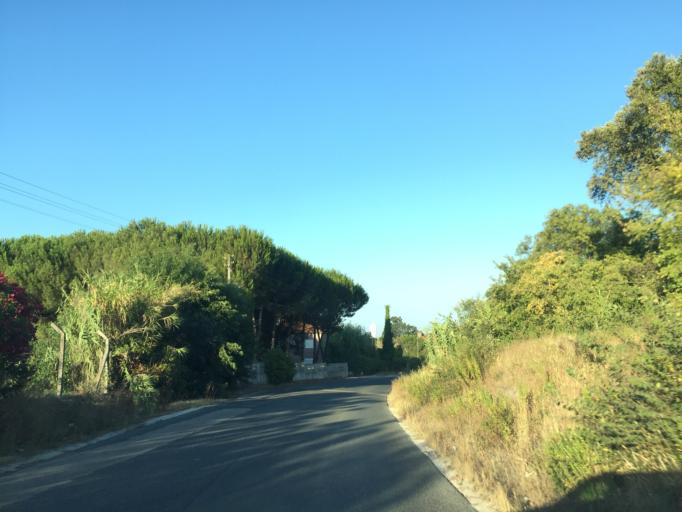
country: PT
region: Santarem
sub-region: Cartaxo
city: Cartaxo
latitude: 39.1671
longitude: -8.8040
